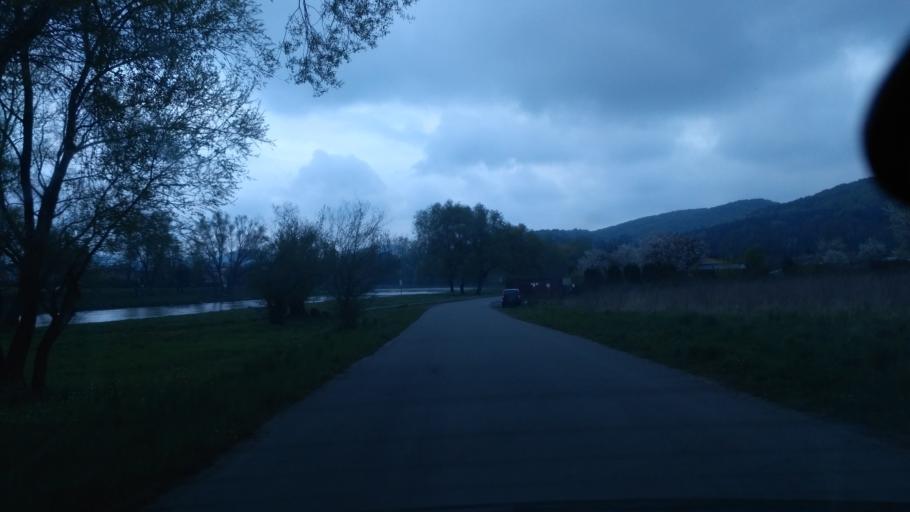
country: PL
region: Subcarpathian Voivodeship
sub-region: Powiat sanocki
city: Sanok
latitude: 49.5679
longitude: 22.2088
